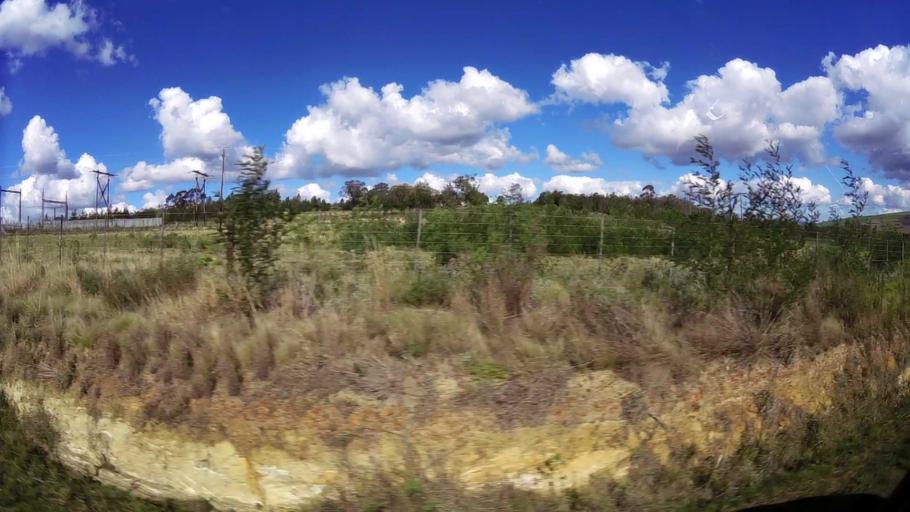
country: ZA
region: Western Cape
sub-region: Overberg District Municipality
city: Swellendam
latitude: -34.0253
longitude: 20.4253
